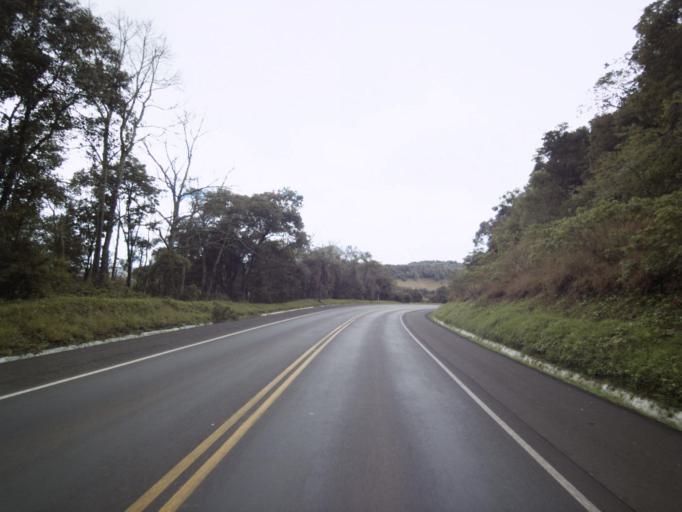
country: BR
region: Santa Catarina
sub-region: Concordia
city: Concordia
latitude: -27.3048
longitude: -51.9817
